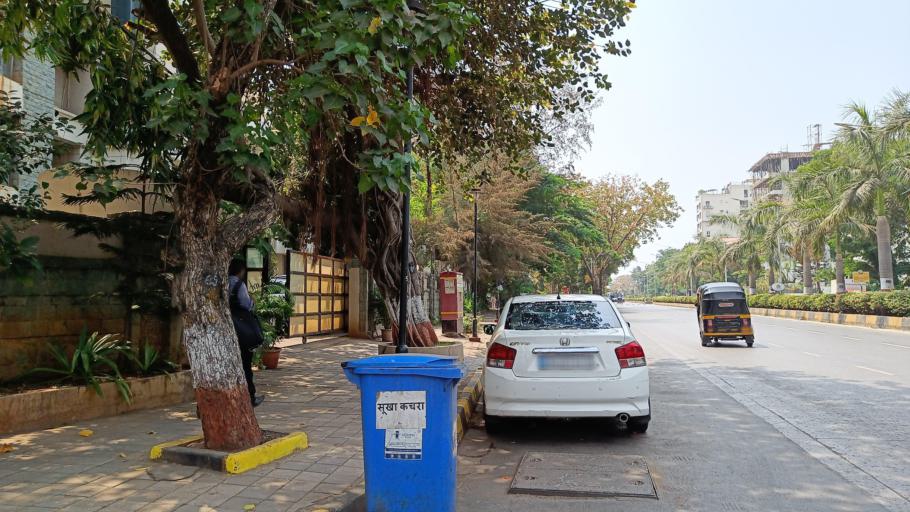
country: IN
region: Maharashtra
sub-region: Mumbai Suburban
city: Mumbai
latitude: 19.1071
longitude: 72.8301
